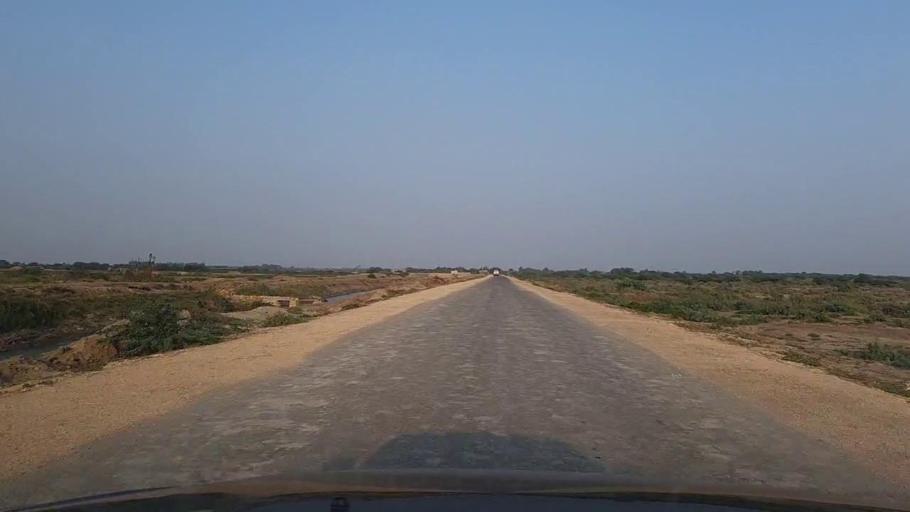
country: PK
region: Sindh
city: Mirpur Sakro
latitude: 24.4441
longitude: 67.7848
